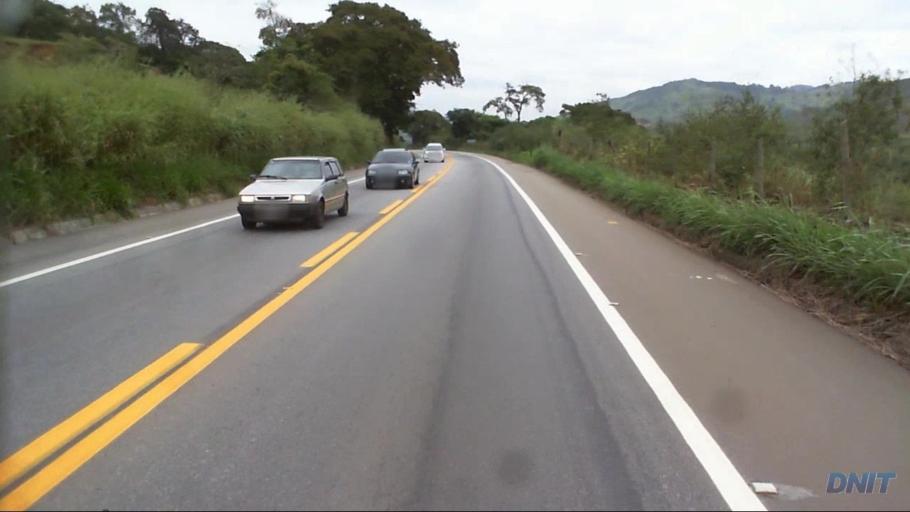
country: BR
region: Minas Gerais
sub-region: Timoteo
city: Timoteo
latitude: -19.5805
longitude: -42.7258
